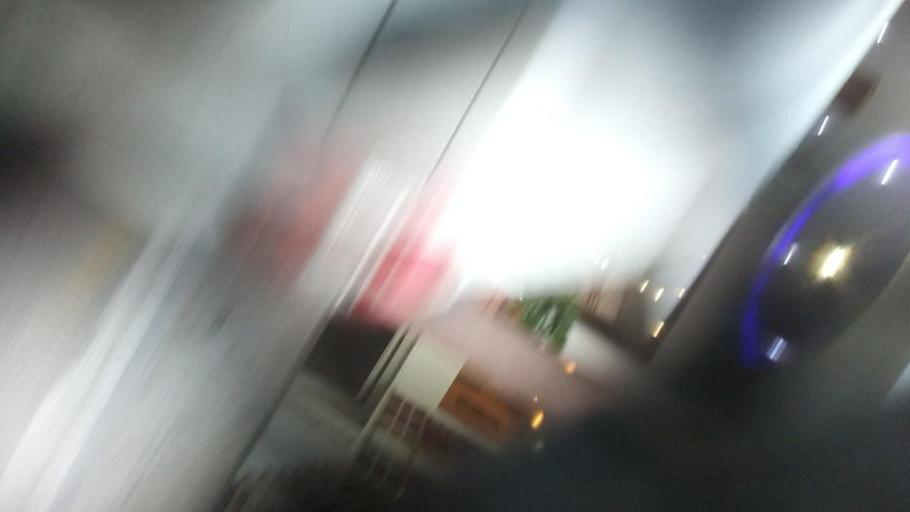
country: AR
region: Jujuy
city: San Salvador de Jujuy
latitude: -24.1861
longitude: -65.3096
